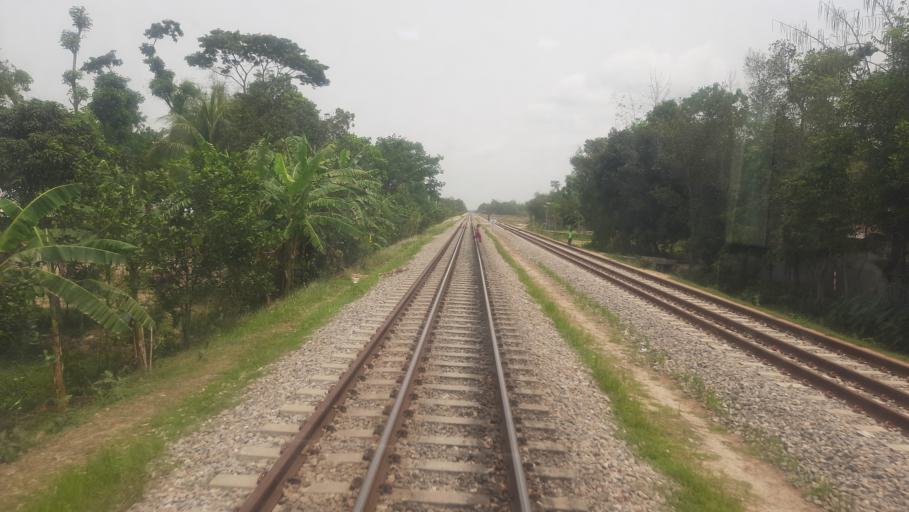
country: IN
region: Tripura
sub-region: West Tripura
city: Agartala
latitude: 23.7045
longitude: 91.1457
